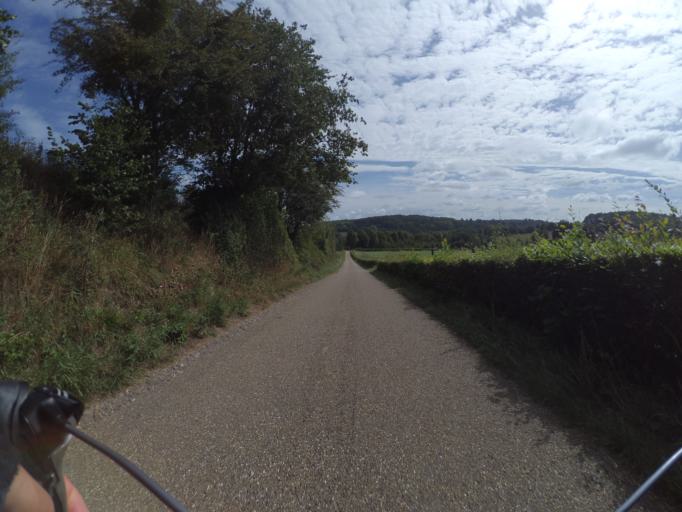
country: NL
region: Limburg
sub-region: Eijsden-Margraten
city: Margraten
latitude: 50.8007
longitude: 5.8598
